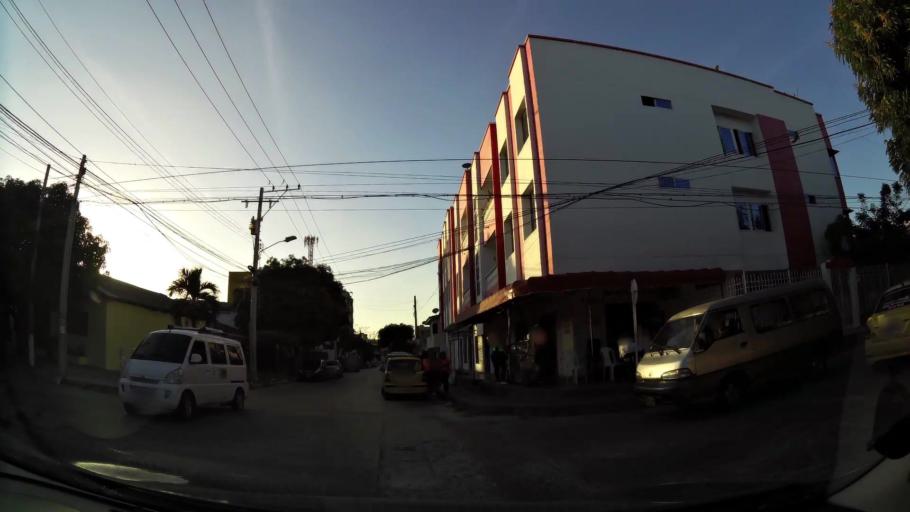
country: CO
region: Atlantico
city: Barranquilla
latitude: 10.9798
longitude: -74.8025
